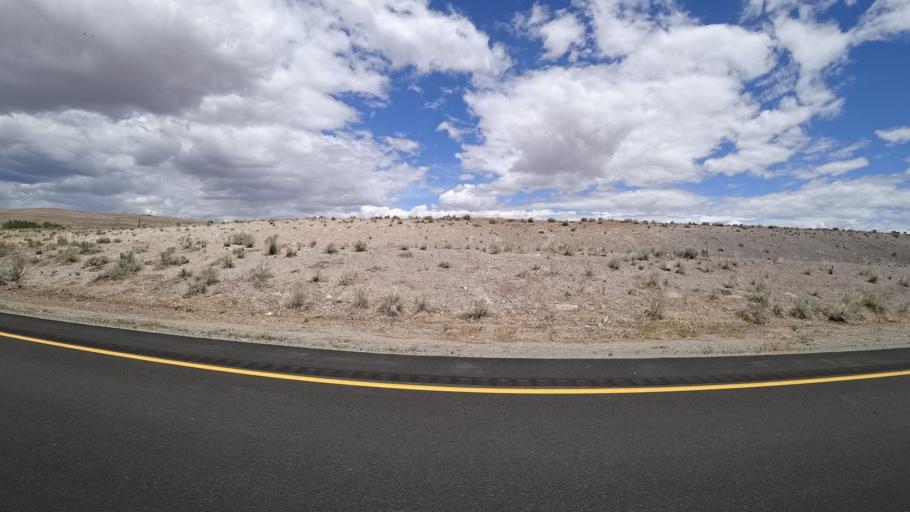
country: US
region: California
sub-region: Inyo County
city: West Bishop
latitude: 37.4372
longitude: -118.5693
